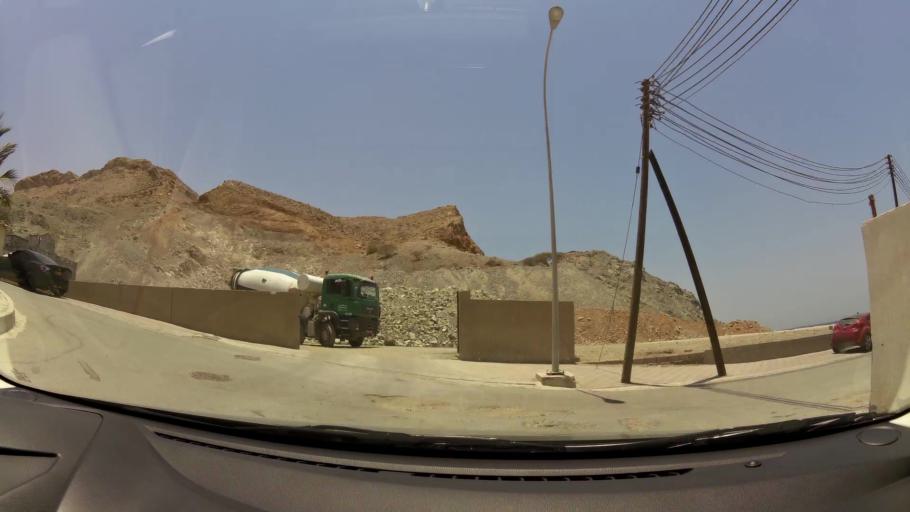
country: OM
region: Muhafazat Masqat
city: Muscat
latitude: 23.6314
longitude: 58.5400
